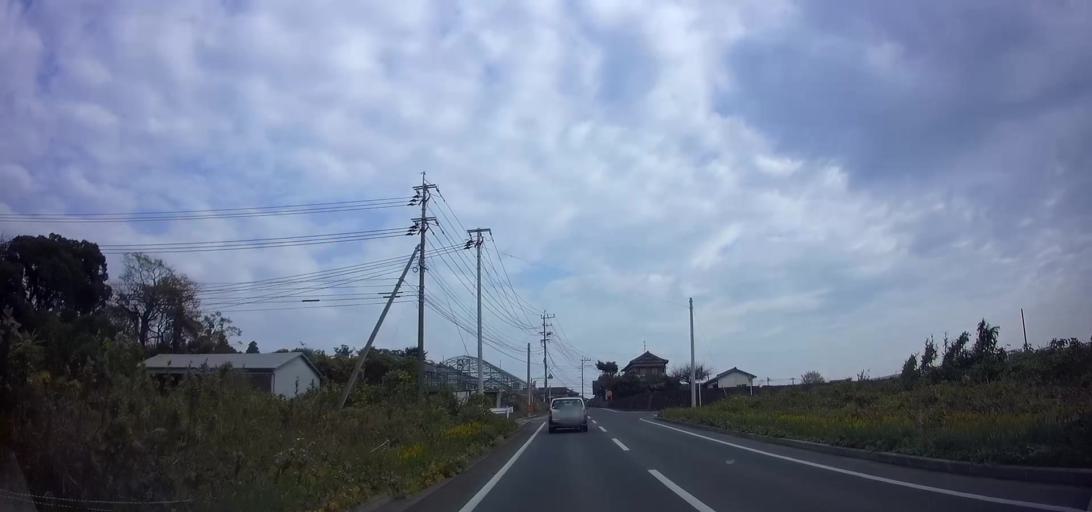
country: JP
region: Nagasaki
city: Shimabara
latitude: 32.6974
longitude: 130.3275
